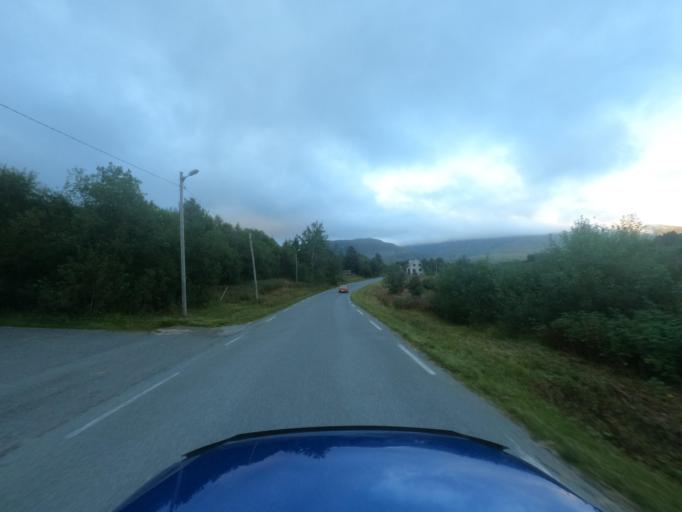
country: NO
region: Nordland
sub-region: Vestvagoy
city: Evjen
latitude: 68.2533
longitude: 13.7742
